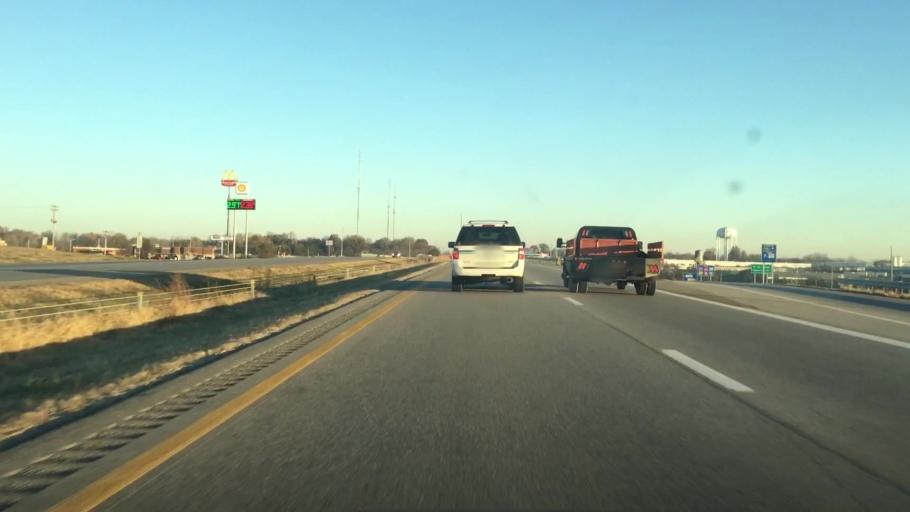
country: US
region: Missouri
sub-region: Buchanan County
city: Saint Joseph
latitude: 39.7219
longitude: -94.7887
